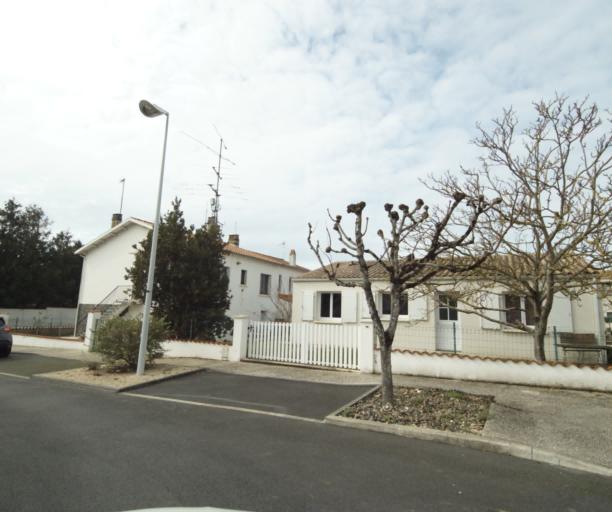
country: FR
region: Poitou-Charentes
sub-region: Departement de la Charente-Maritime
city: Lagord
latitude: 46.1897
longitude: -1.1571
